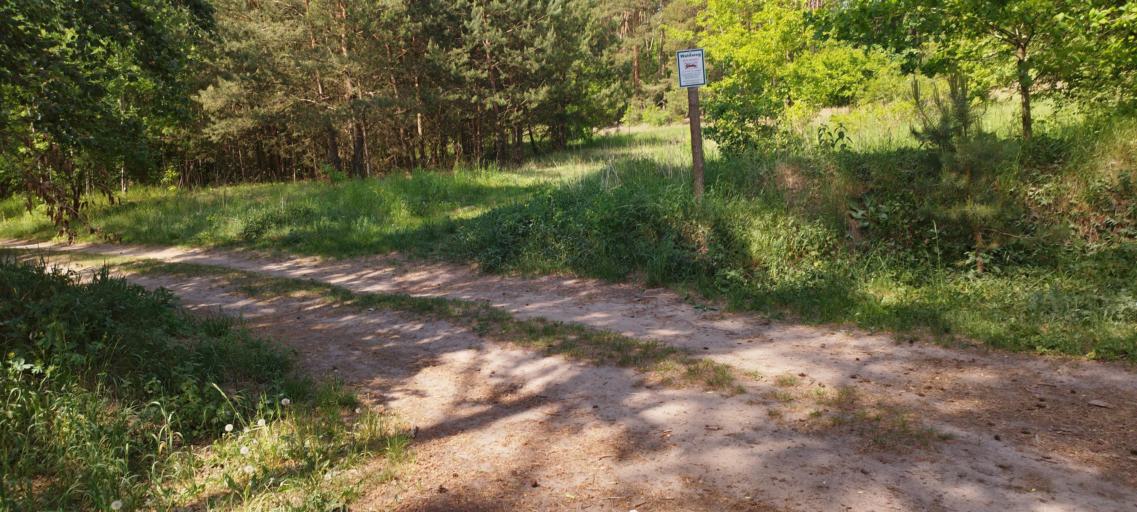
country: DE
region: Brandenburg
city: Furstenwalde
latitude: 52.3833
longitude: 14.0395
